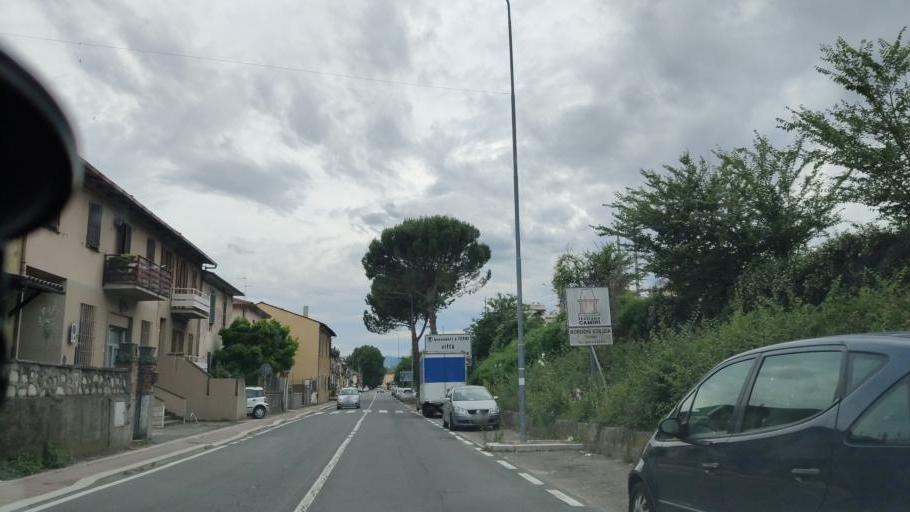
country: IT
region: Umbria
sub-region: Provincia di Terni
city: Terni
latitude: 42.5744
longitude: 12.6710
